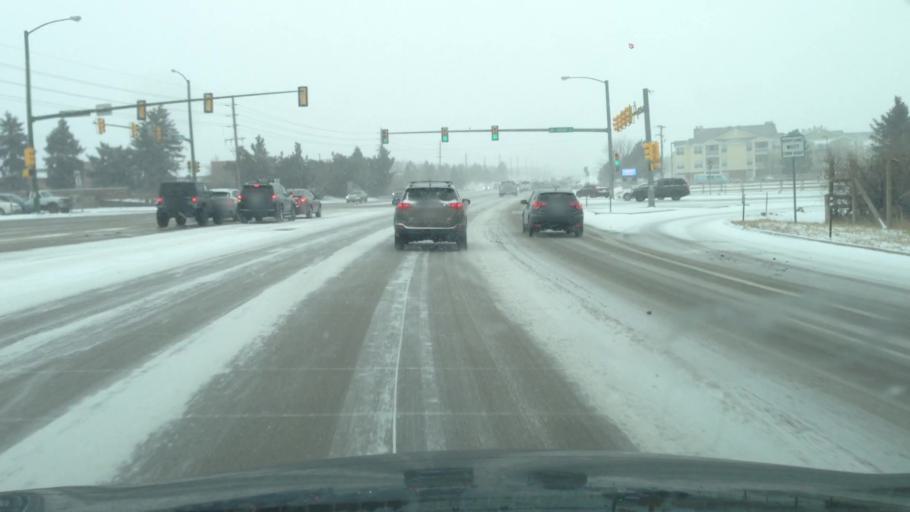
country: US
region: Colorado
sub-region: Arapahoe County
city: Dove Valley
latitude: 39.6109
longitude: -104.8111
